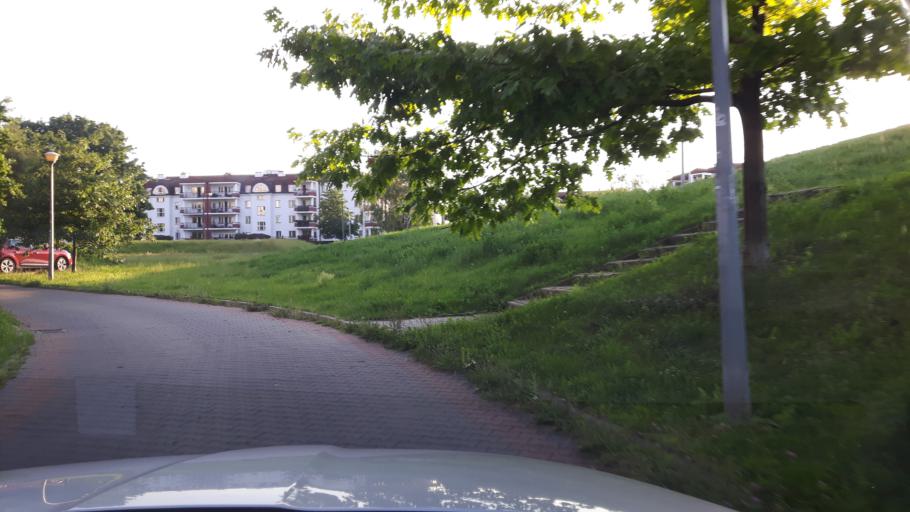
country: PL
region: Masovian Voivodeship
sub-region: Warszawa
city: Ursynow
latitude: 52.1634
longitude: 21.0227
